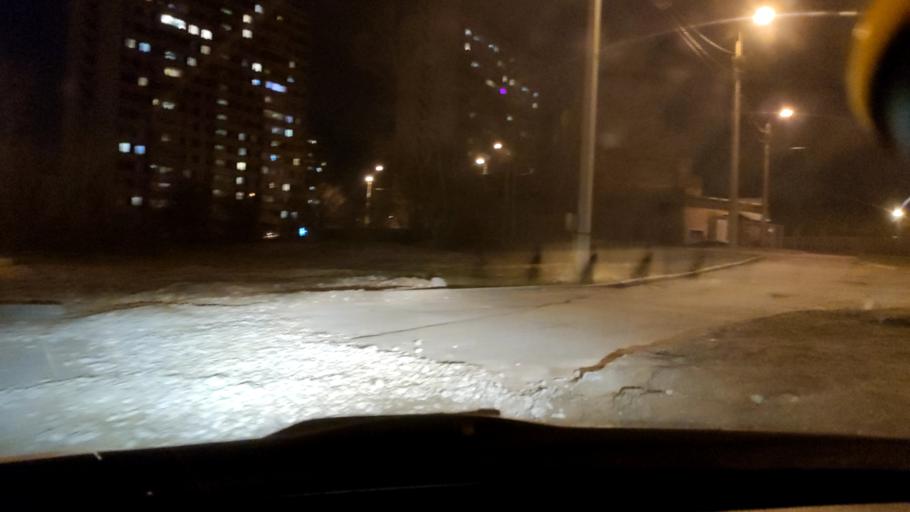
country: RU
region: Samara
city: Zhigulevsk
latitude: 53.4796
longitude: 49.5262
